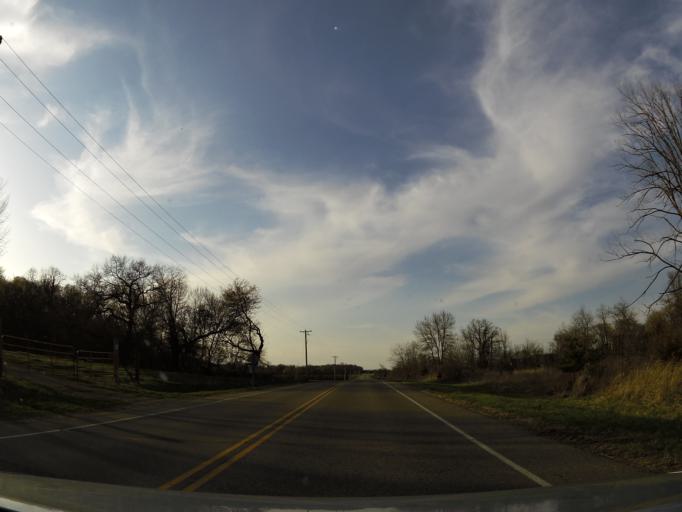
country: US
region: Wisconsin
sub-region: Pierce County
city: River Falls
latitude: 44.8946
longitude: -92.6702
